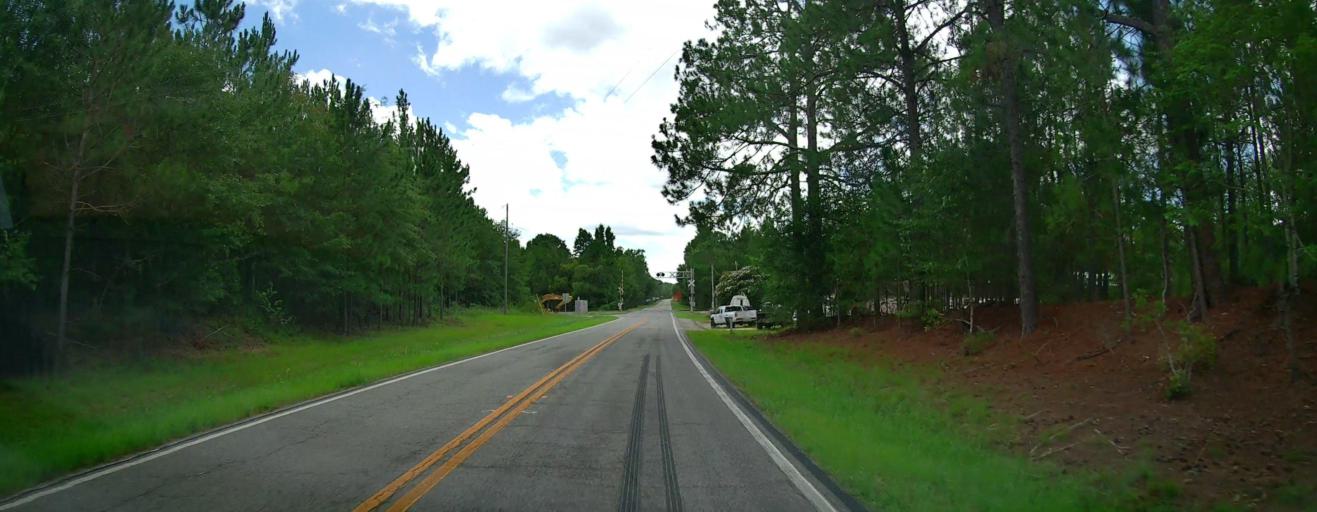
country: US
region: Georgia
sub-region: Wilcox County
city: Rochelle
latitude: 31.8599
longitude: -83.5583
